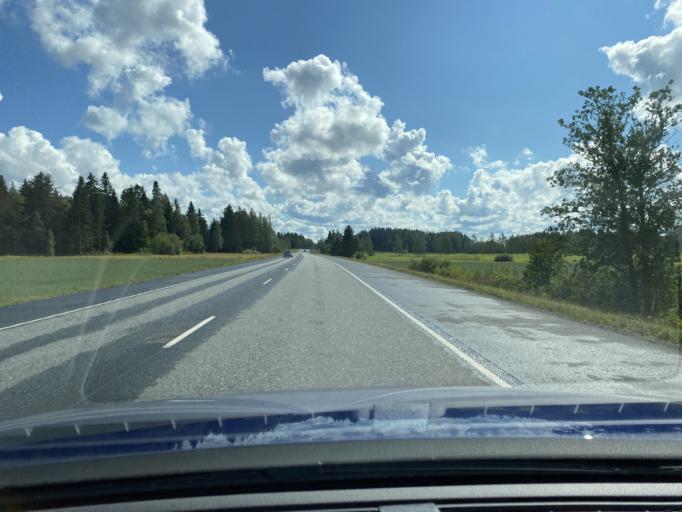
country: FI
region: Pirkanmaa
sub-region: Tampere
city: Lempaeaelae
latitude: 61.3315
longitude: 23.7772
